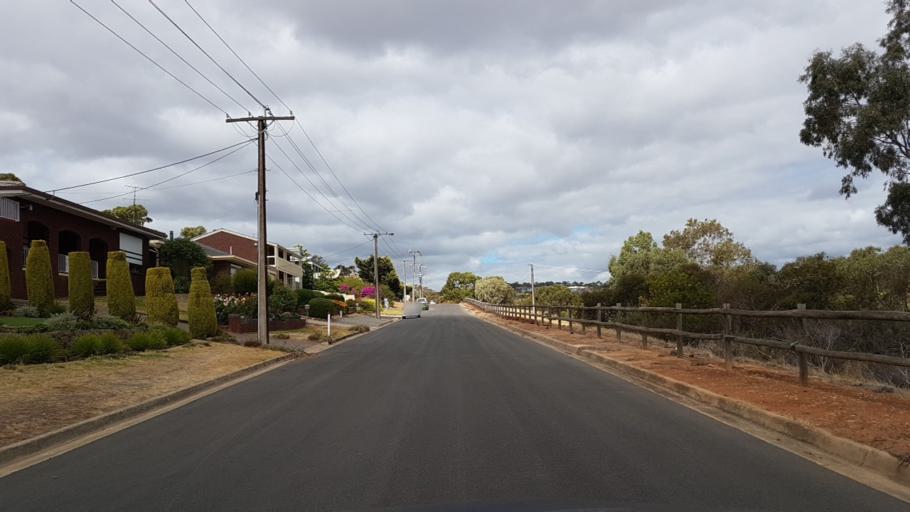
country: AU
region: South Australia
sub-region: Gawler
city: Gawler
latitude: -34.6084
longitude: 138.7522
